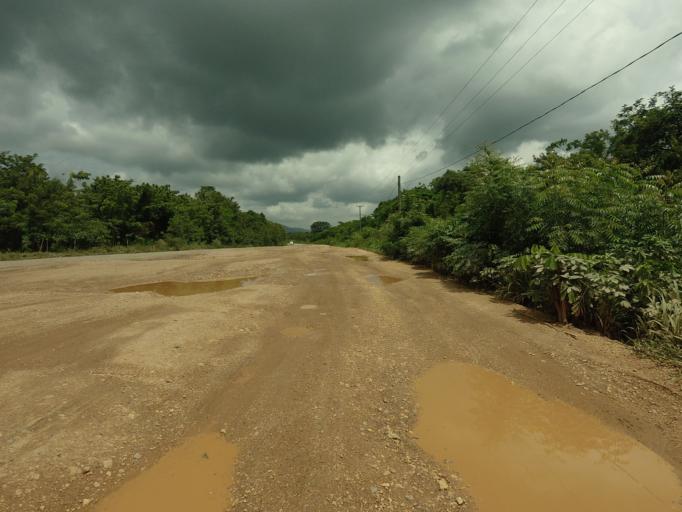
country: GH
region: Volta
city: Ho
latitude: 6.6471
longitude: 0.2991
